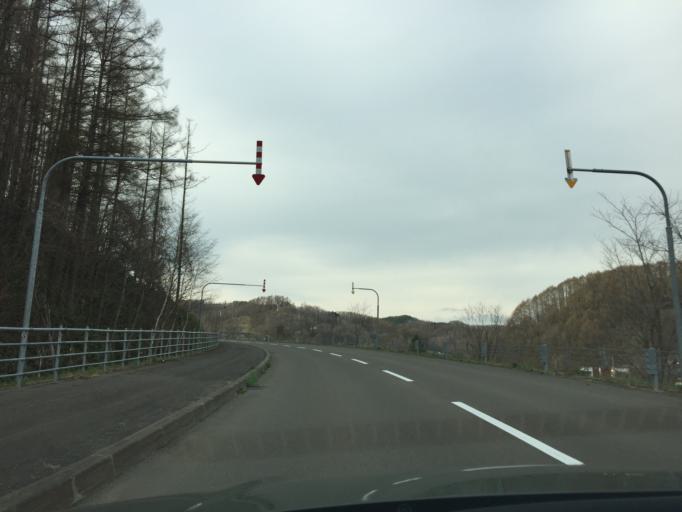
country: JP
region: Hokkaido
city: Utashinai
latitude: 43.5125
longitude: 142.0260
